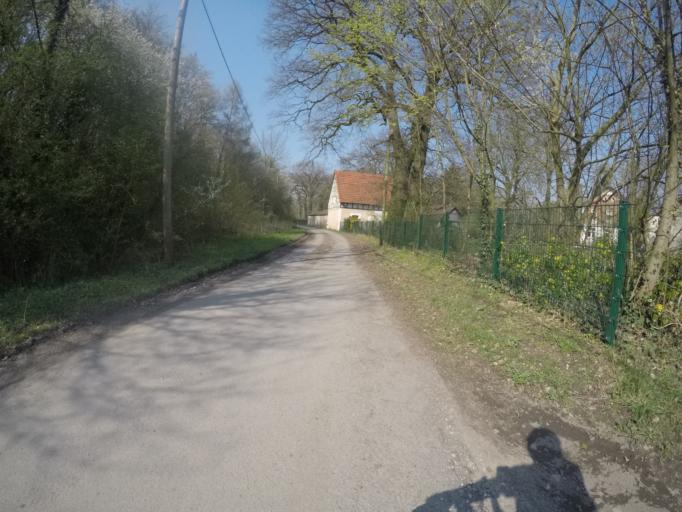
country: DE
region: North Rhine-Westphalia
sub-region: Regierungsbezirk Detmold
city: Bielefeld
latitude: 52.0423
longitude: 8.6095
